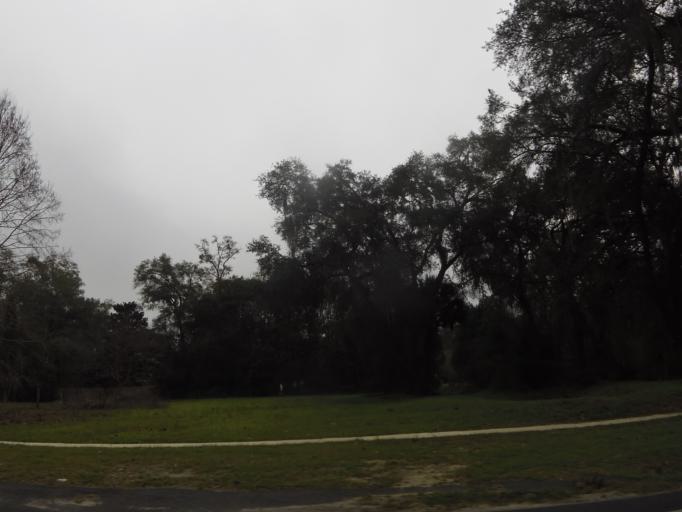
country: US
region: Florida
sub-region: Alachua County
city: High Springs
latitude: 29.8325
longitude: -82.5937
